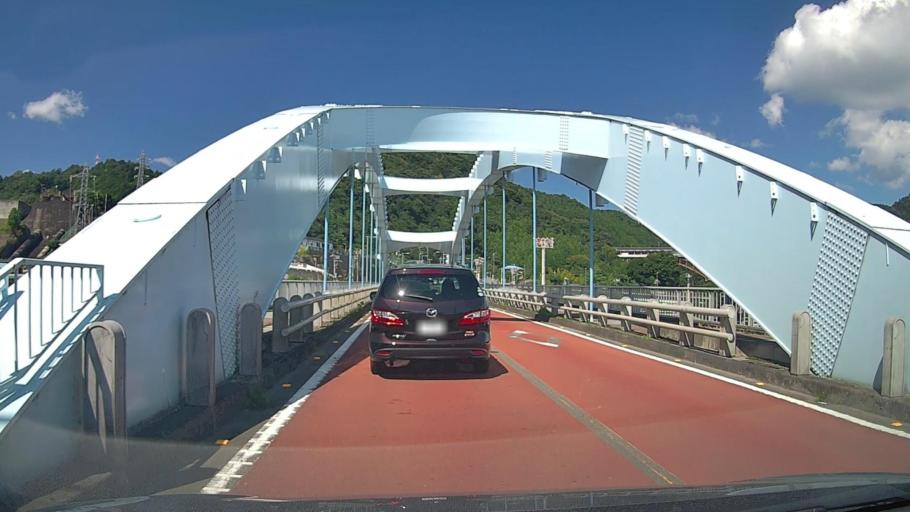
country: JP
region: Kanagawa
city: Odawara
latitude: 35.3558
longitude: 139.0696
